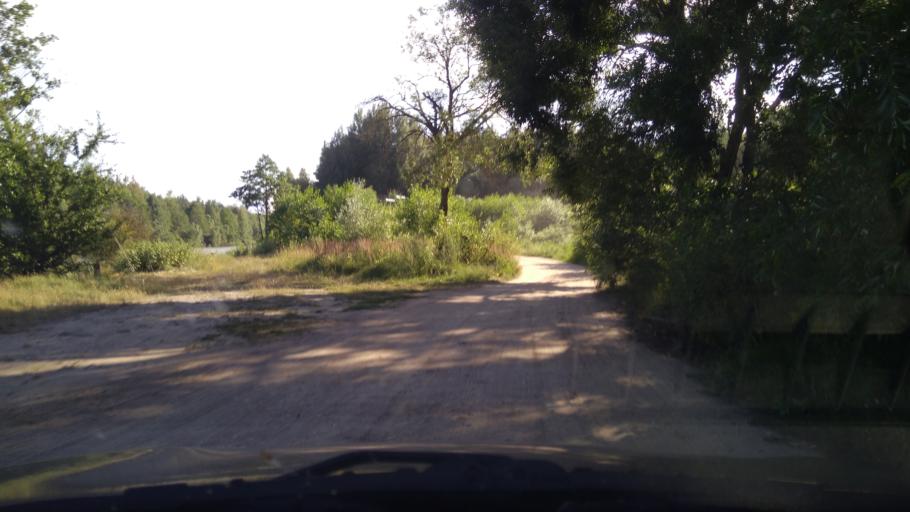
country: BY
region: Brest
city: Byelaazyorsk
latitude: 52.4449
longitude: 25.1758
